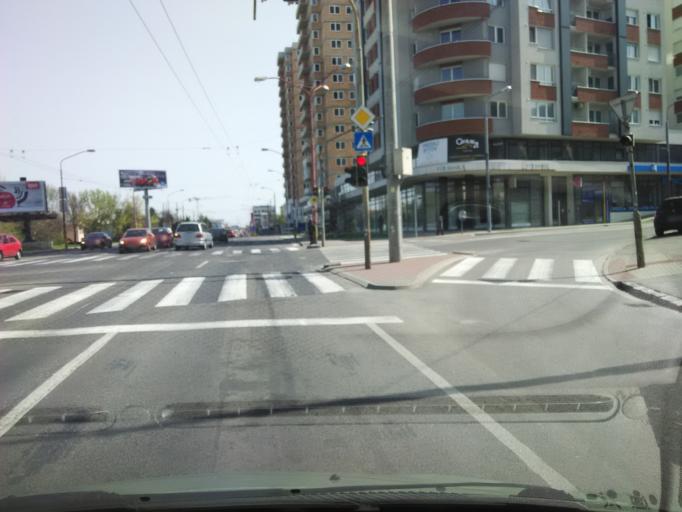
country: SK
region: Bratislavsky
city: Bratislava
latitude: 48.1501
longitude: 17.1657
